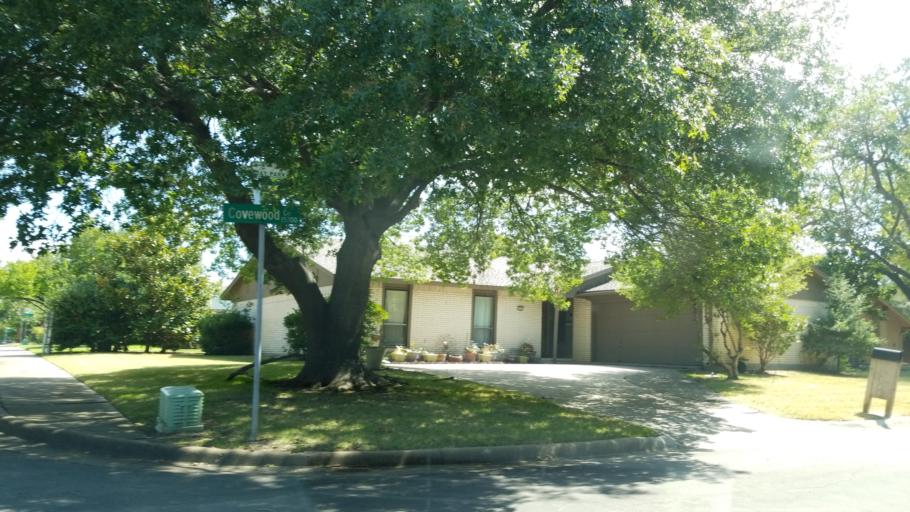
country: US
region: Texas
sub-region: Dallas County
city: Addison
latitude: 32.9645
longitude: -96.7806
